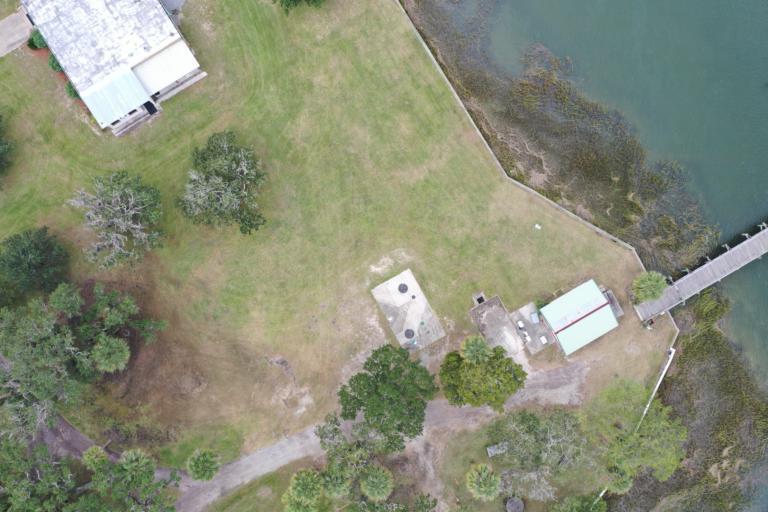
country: US
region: Georgia
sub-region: Chatham County
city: Whitemarsh Island
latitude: 31.9898
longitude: -81.0214
